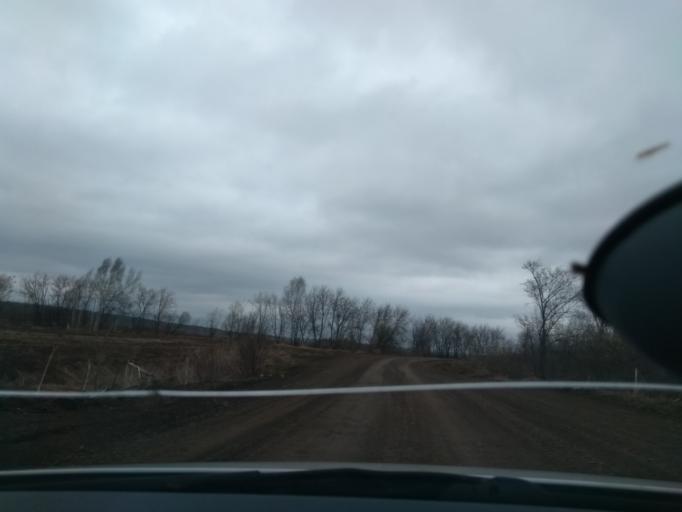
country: RU
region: Perm
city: Orda
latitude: 57.2464
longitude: 56.6115
